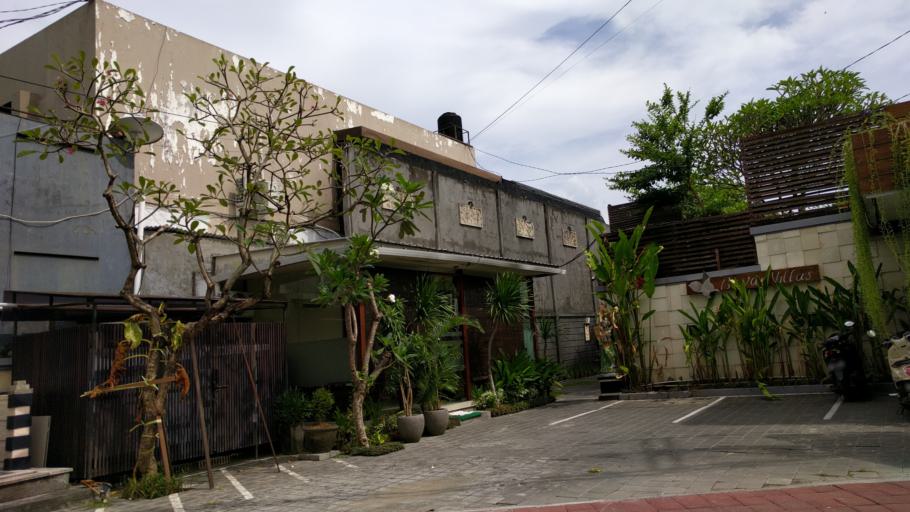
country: ID
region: Bali
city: Kuta
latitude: -8.6726
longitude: 115.1556
